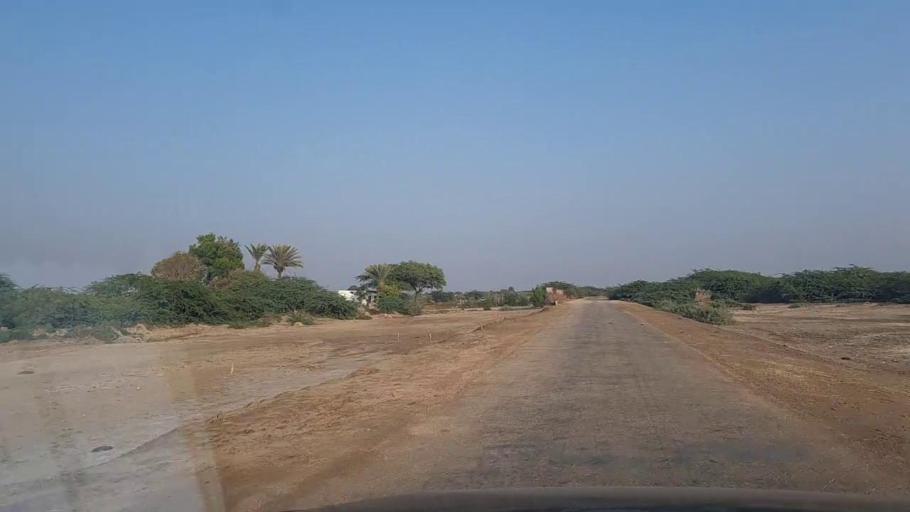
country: PK
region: Sindh
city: Keti Bandar
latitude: 24.2656
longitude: 67.5600
